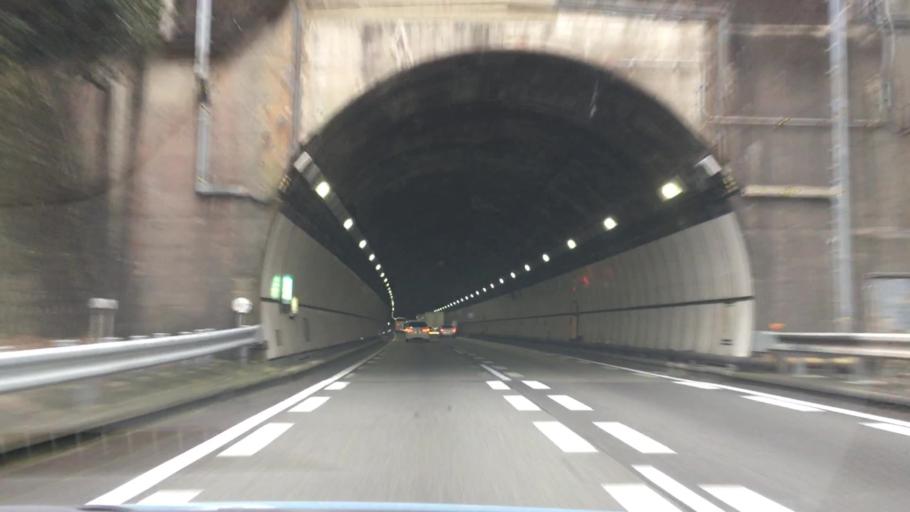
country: JP
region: Shizuoka
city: Shizuoka-shi
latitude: 35.0590
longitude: 138.5203
